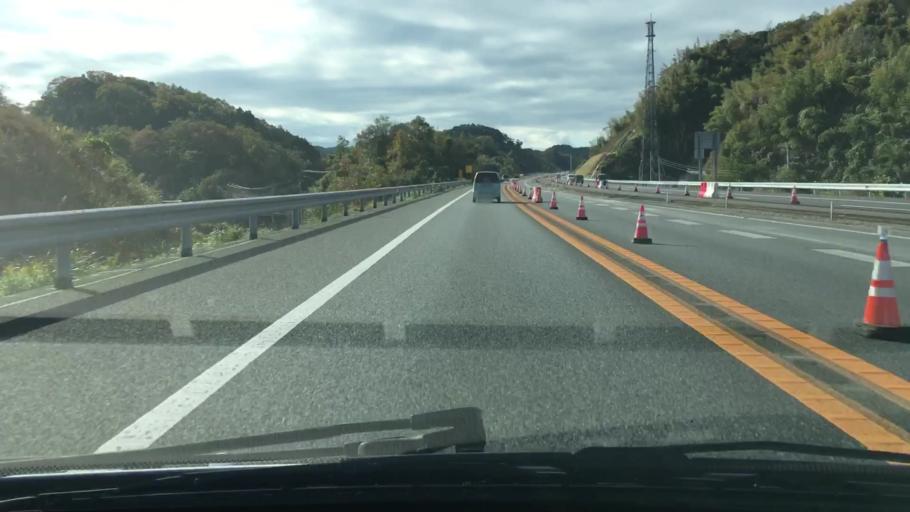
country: JP
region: Chiba
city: Kimitsu
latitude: 35.2800
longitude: 139.9247
